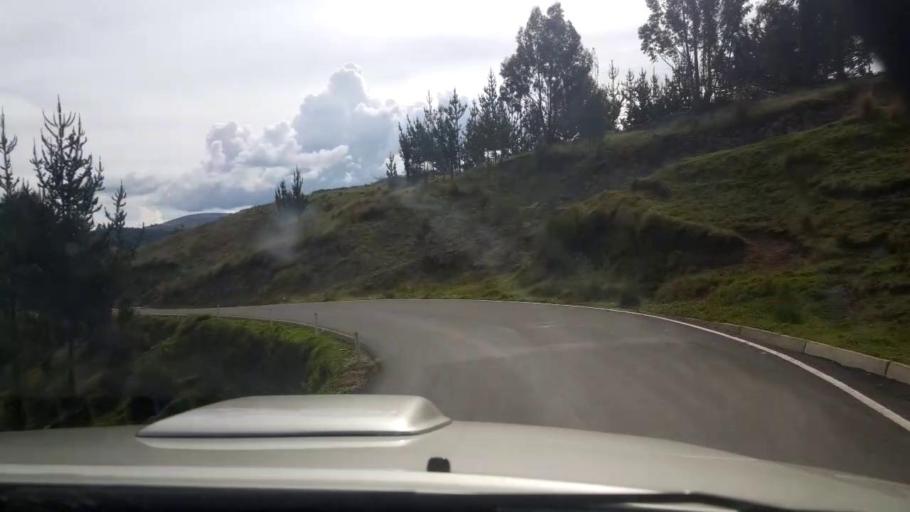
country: PE
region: Ayacucho
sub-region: Provincia de Cangallo
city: Pampa Cangallo
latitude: -13.4487
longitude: -74.1978
